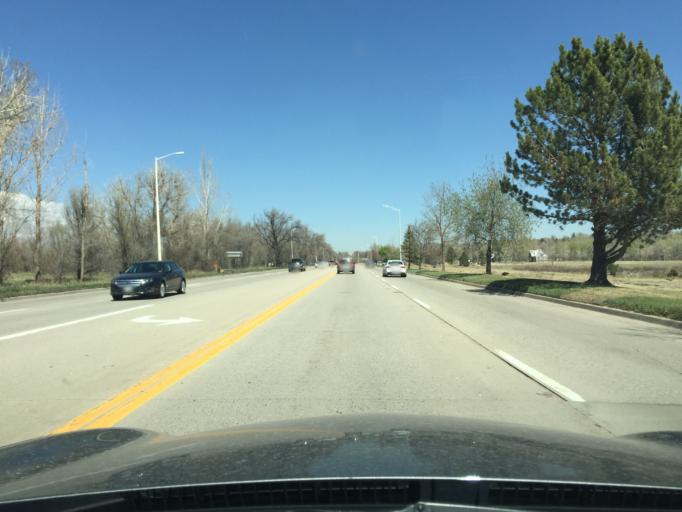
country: US
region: Colorado
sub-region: Boulder County
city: Longmont
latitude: 40.1606
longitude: -105.1306
